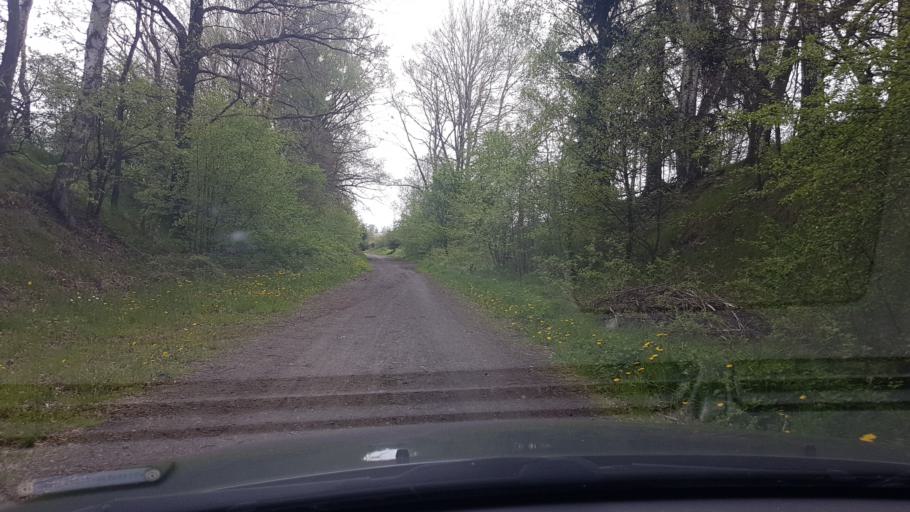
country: CZ
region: Karlovarsky
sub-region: Okres Cheb
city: Cheb
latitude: 50.0528
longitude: 12.3877
